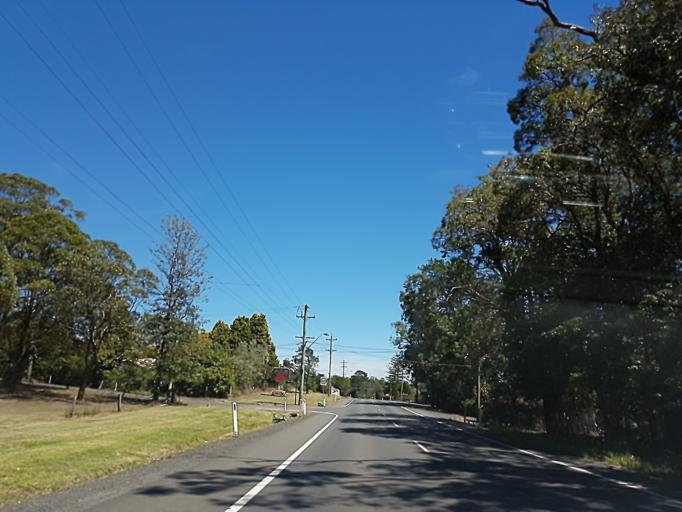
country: AU
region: New South Wales
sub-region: Hornsby Shire
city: Glenorie
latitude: -33.6071
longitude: 151.0161
